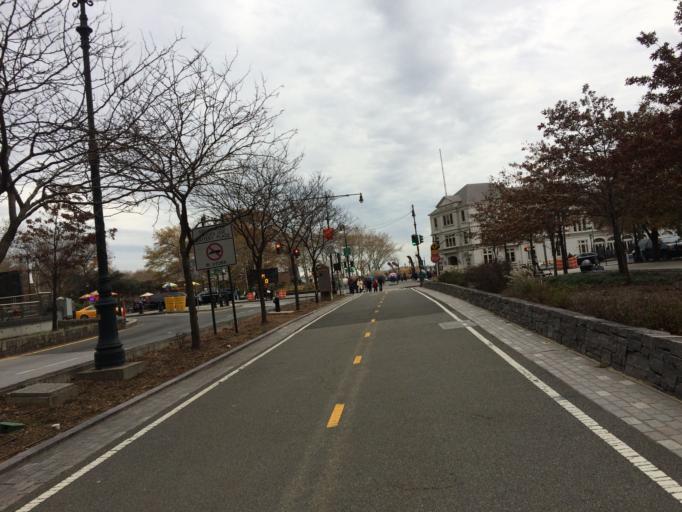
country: US
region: New York
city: New York City
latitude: 40.7054
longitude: -74.0169
